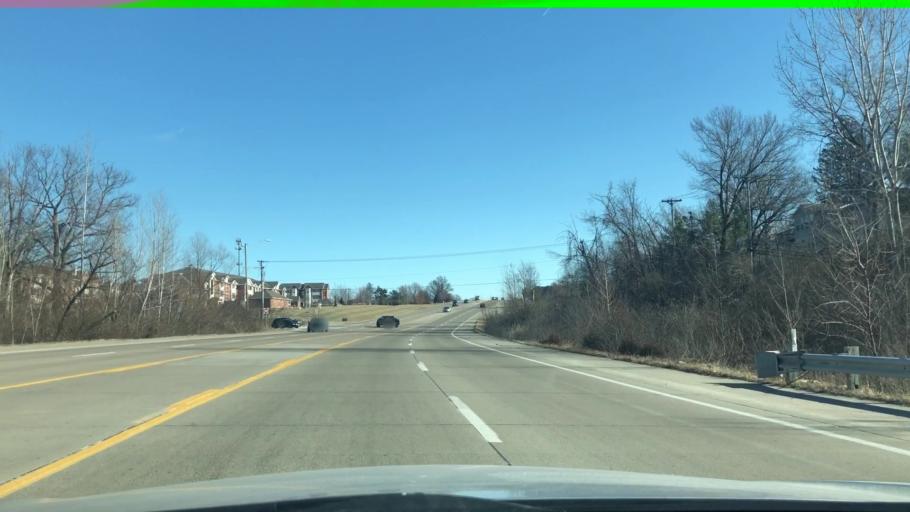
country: US
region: Missouri
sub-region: Boone County
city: Columbia
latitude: 38.9558
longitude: -92.3933
